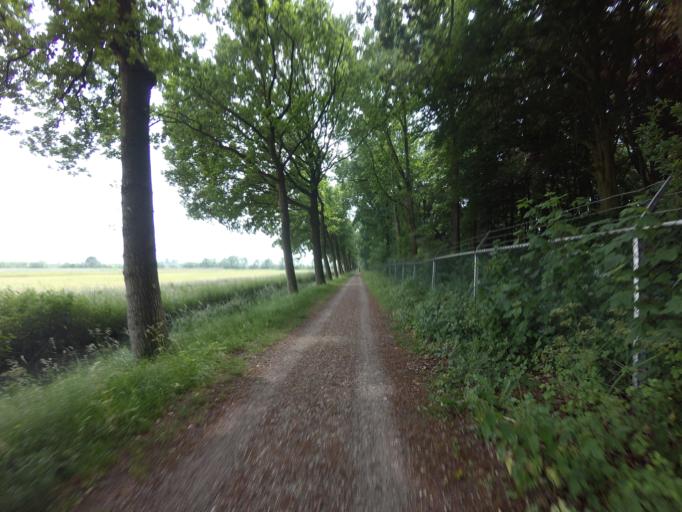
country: NL
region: Utrecht
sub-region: Stichtse Vecht
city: Spechtenkamp
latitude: 52.1137
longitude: 4.9944
